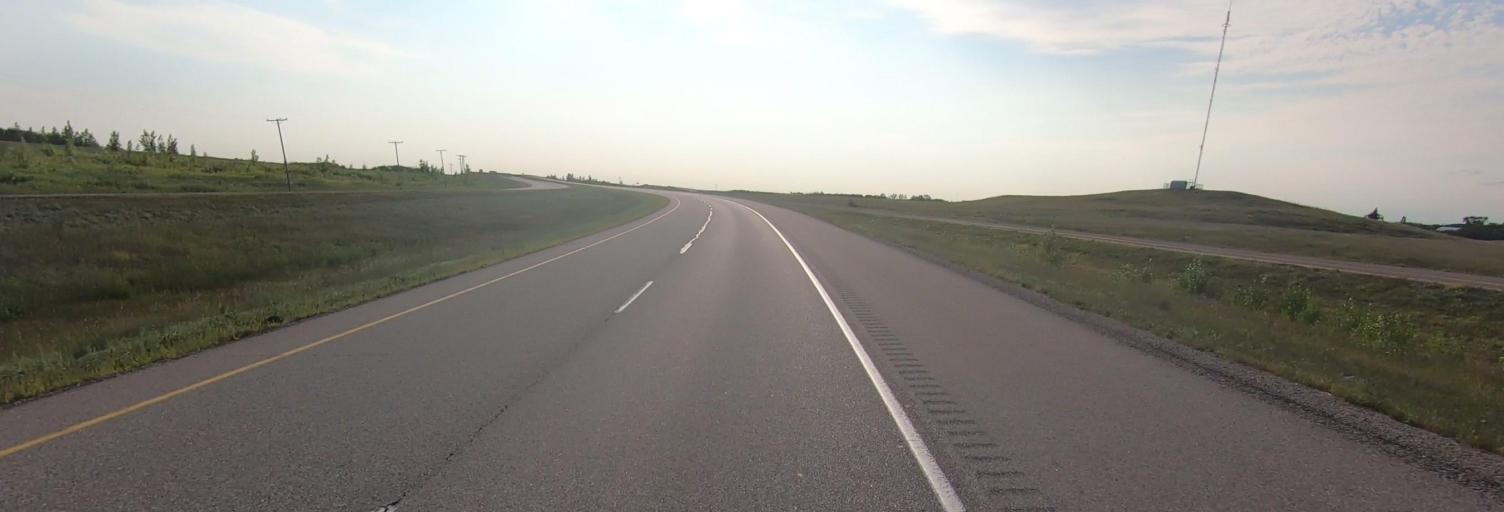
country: CA
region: Saskatchewan
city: Melville
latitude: 50.3850
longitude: -102.5939
